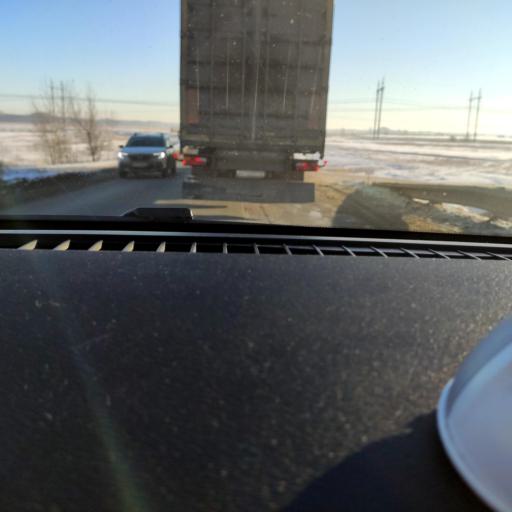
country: RU
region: Samara
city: Spiridonovka
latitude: 53.1429
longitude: 50.5911
